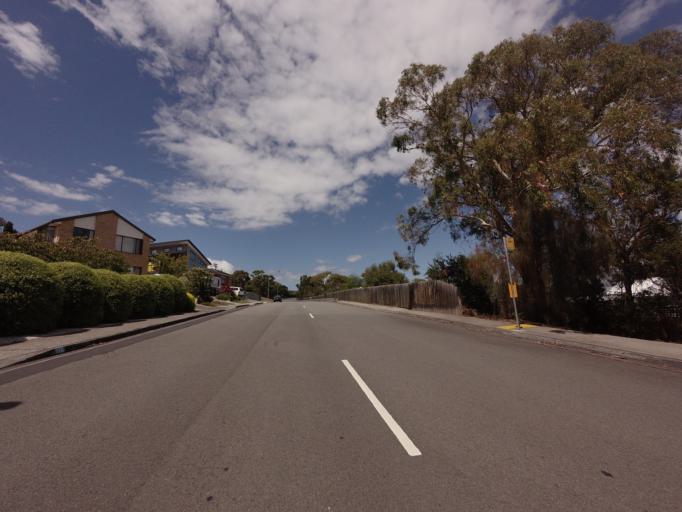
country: AU
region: Tasmania
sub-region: Clarence
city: Howrah
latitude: -42.8940
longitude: 147.4143
